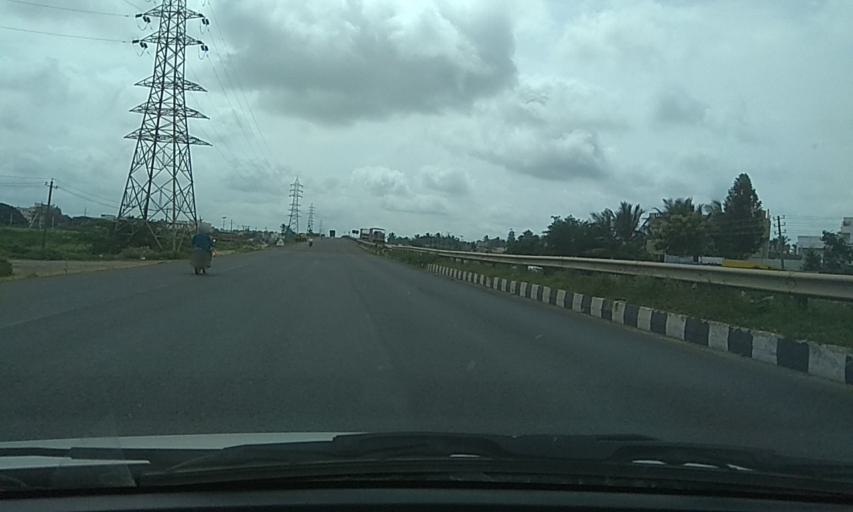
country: IN
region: Karnataka
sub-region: Davanagere
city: Harihar
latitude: 14.4430
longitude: 75.8954
